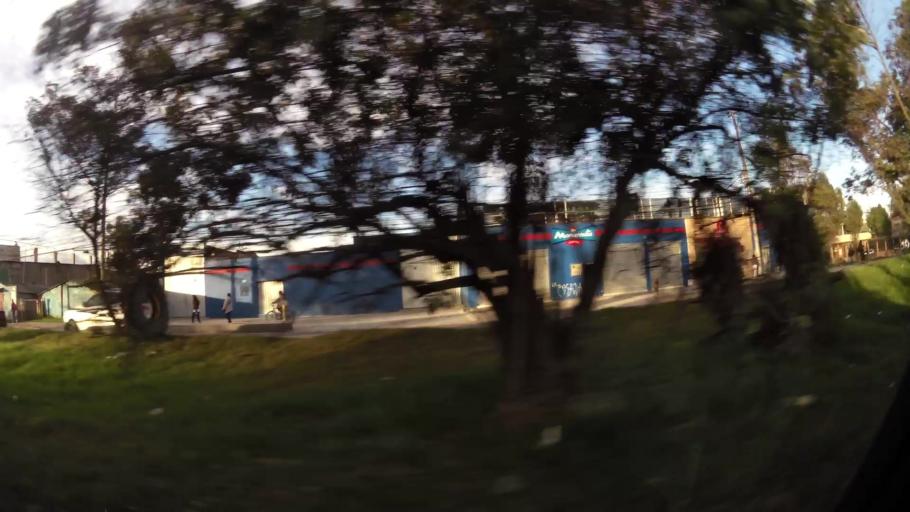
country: CO
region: Cundinamarca
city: Funza
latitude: 4.6911
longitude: -74.1650
